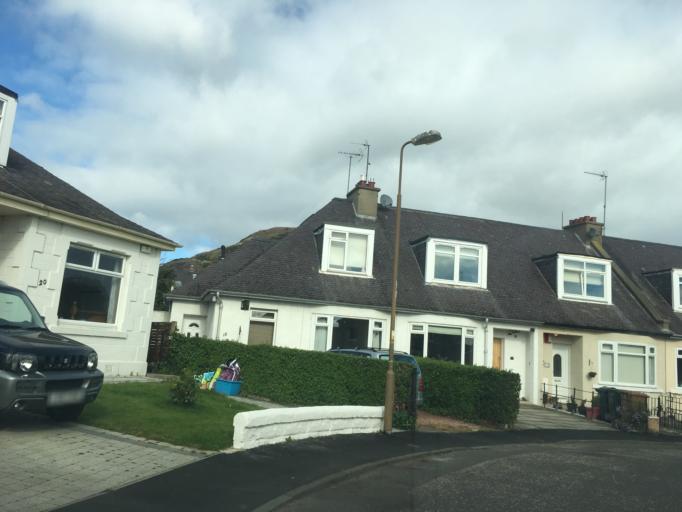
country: GB
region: Scotland
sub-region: West Lothian
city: Seafield
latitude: 55.9347
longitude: -3.1615
